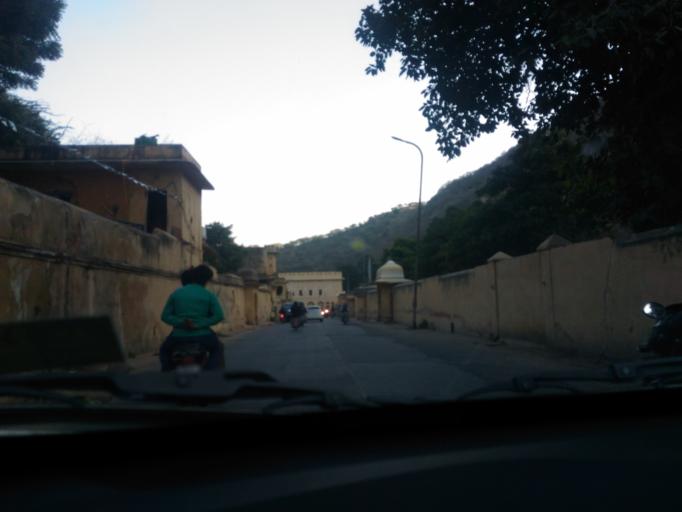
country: IN
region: Rajasthan
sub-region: Jaipur
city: Jaipur
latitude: 26.9003
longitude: 75.8538
